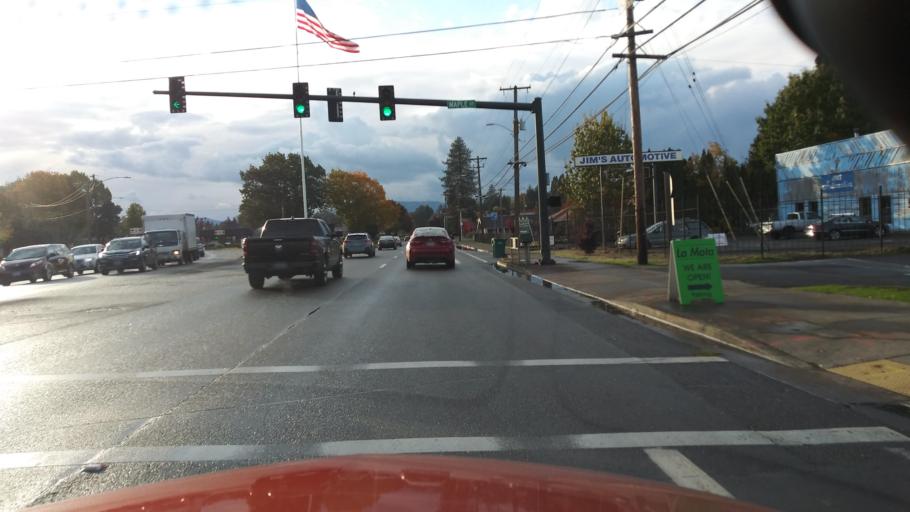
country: US
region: Oregon
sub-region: Washington County
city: Forest Grove
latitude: 45.5202
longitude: -123.0909
